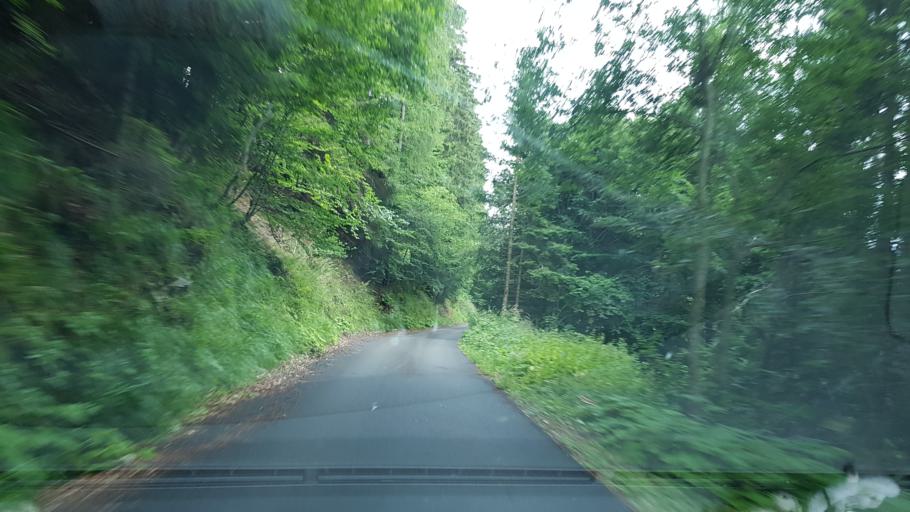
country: IT
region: Friuli Venezia Giulia
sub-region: Provincia di Udine
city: Cercivento
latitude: 46.5421
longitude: 12.9864
